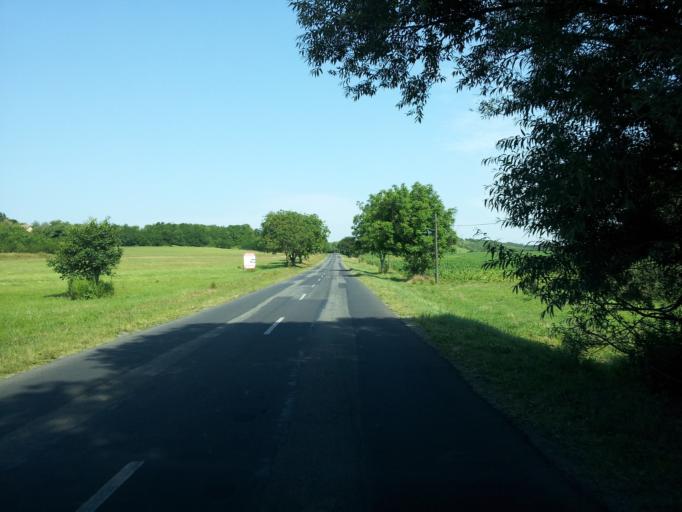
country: HU
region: Zala
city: Cserszegtomaj
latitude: 46.8334
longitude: 17.1918
